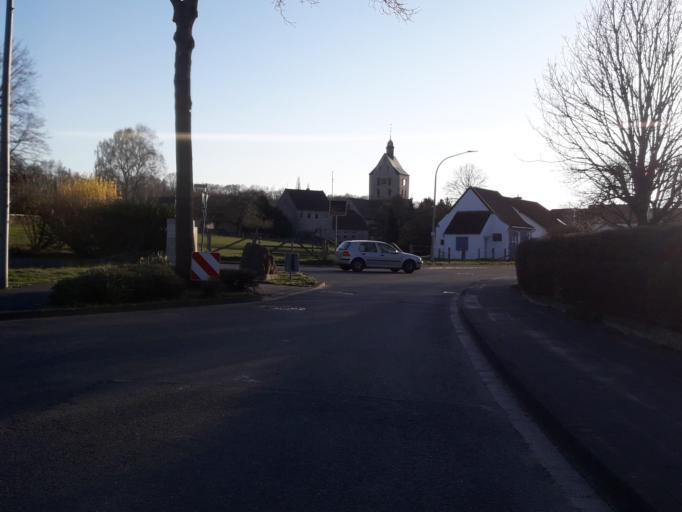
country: DE
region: North Rhine-Westphalia
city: Bad Lippspringe
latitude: 51.7457
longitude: 8.8513
